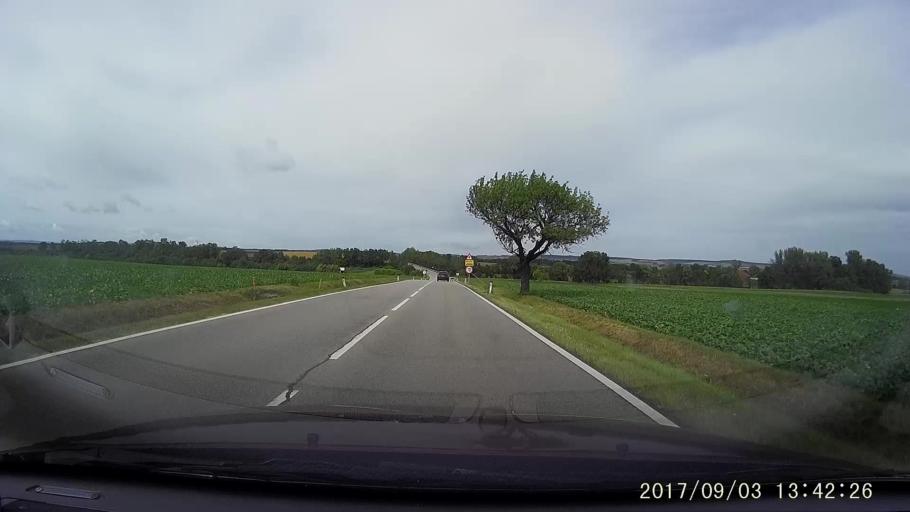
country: AT
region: Lower Austria
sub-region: Politischer Bezirk Hollabrunn
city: Wullersdorf
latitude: 48.6135
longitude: 16.0671
